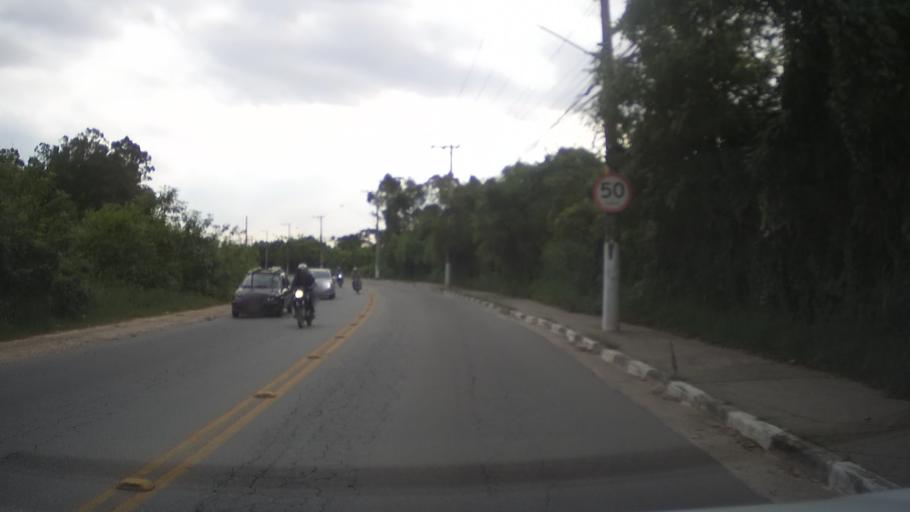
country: BR
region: Sao Paulo
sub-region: Guarulhos
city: Guarulhos
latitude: -23.4207
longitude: -46.4880
